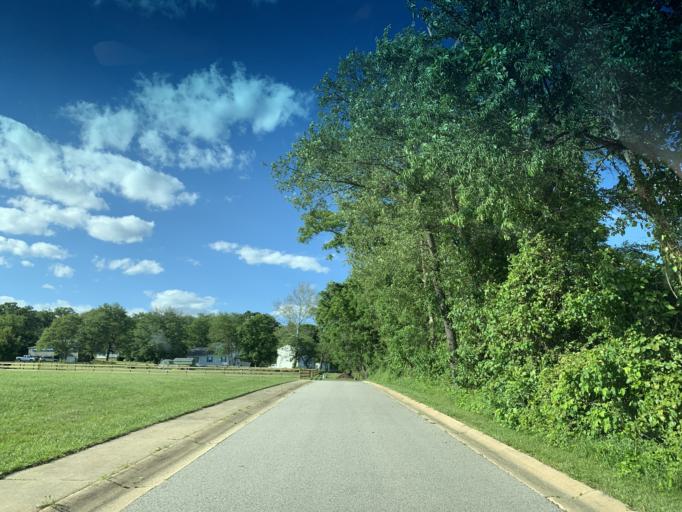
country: US
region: Maryland
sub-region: Cecil County
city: Perryville
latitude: 39.5838
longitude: -76.0621
